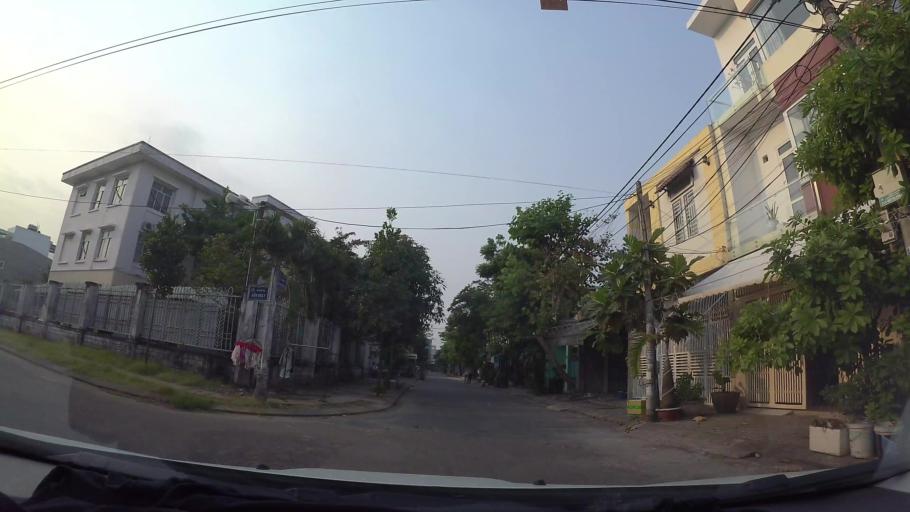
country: VN
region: Da Nang
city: Cam Le
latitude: 16.0183
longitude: 108.1971
